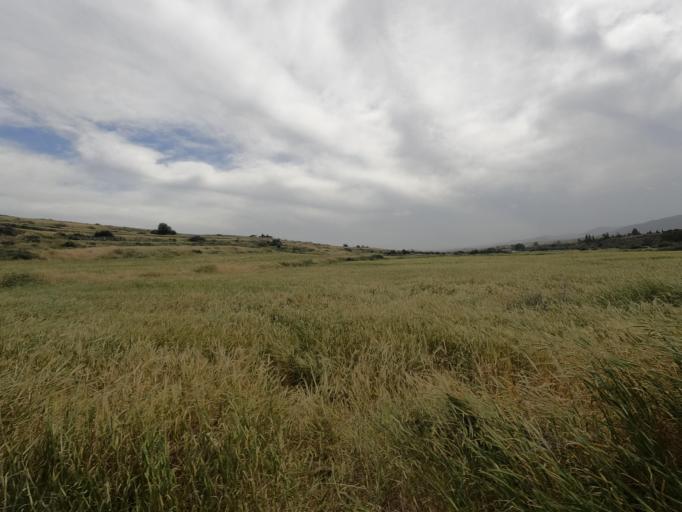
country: CY
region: Lefkosia
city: Astromeritis
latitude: 35.1128
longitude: 32.9697
